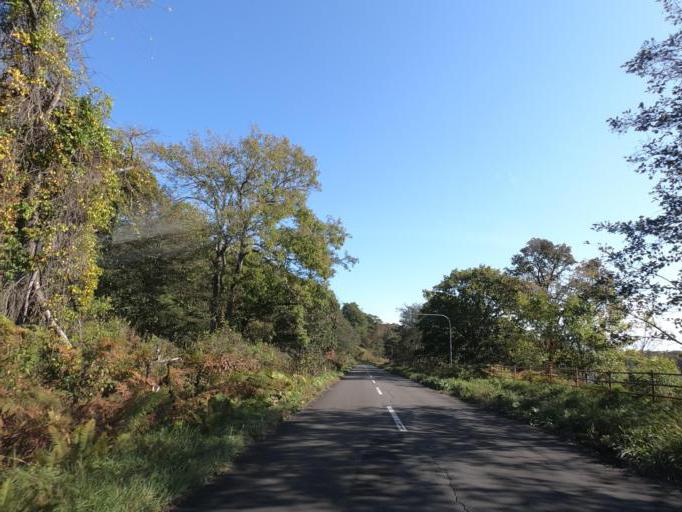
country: JP
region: Hokkaido
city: Obihiro
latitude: 42.6085
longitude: 143.5478
